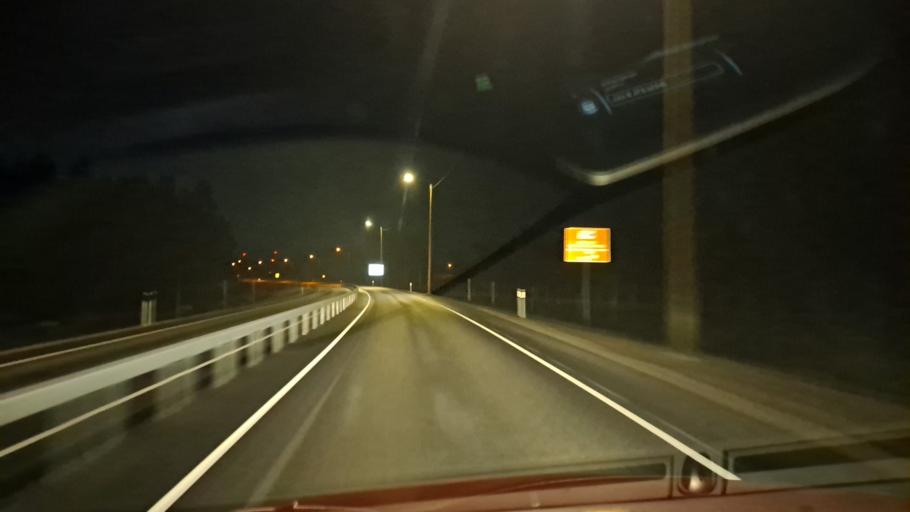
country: FI
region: Lapland
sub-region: Kemi-Tornio
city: Simo
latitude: 65.6551
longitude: 25.0884
